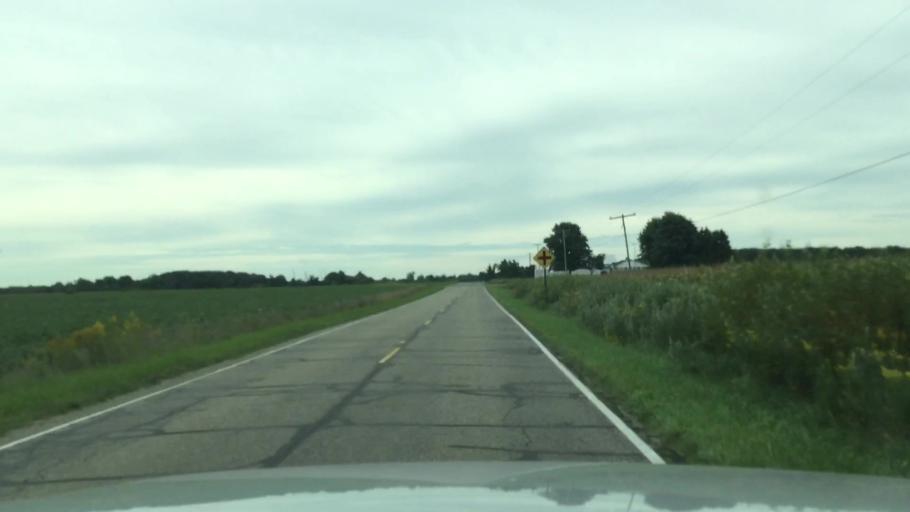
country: US
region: Michigan
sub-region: Genesee County
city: Flushing
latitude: 43.0747
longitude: -83.9877
